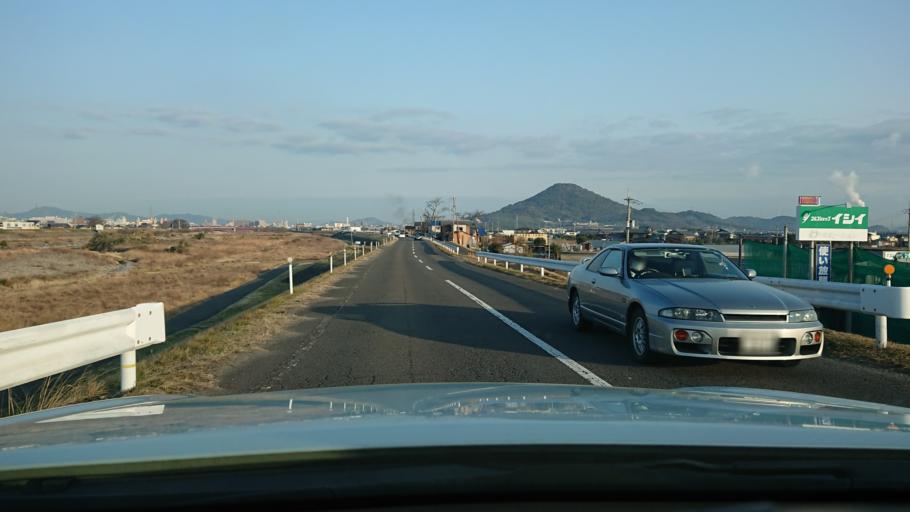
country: JP
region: Kagawa
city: Marugame
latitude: 34.2717
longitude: 133.8287
